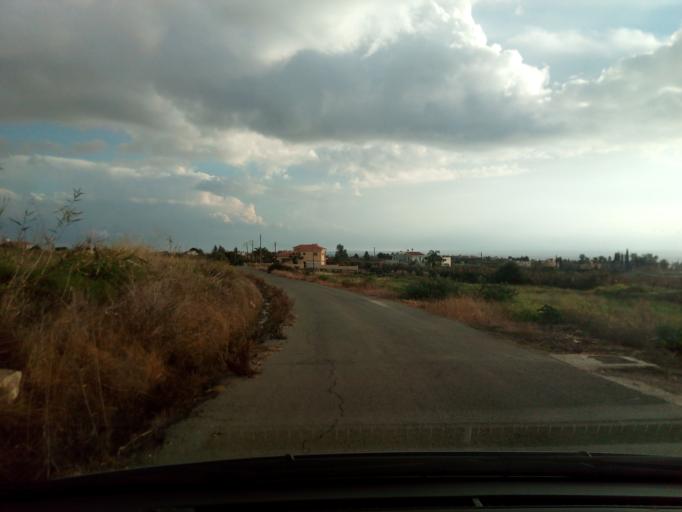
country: CY
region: Pafos
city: Pegeia
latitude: 34.8690
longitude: 32.3687
